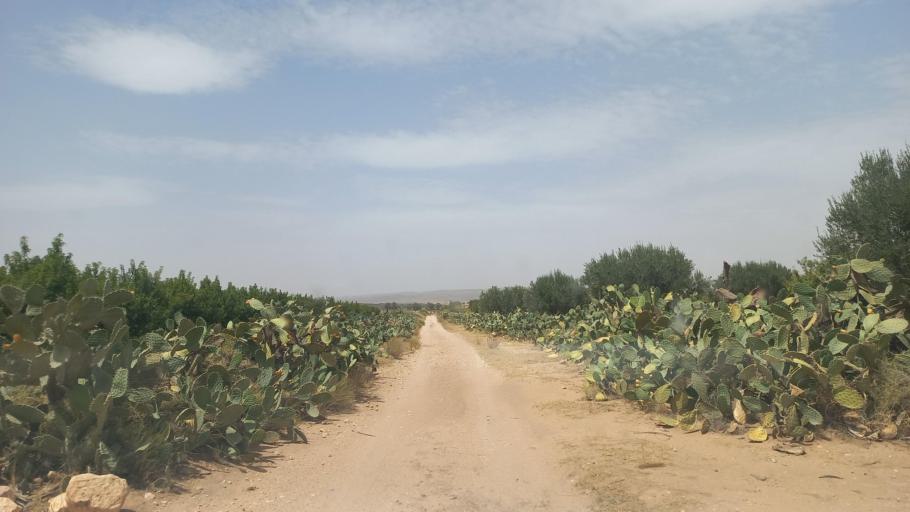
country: TN
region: Al Qasrayn
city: Kasserine
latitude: 35.2615
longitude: 8.9887
